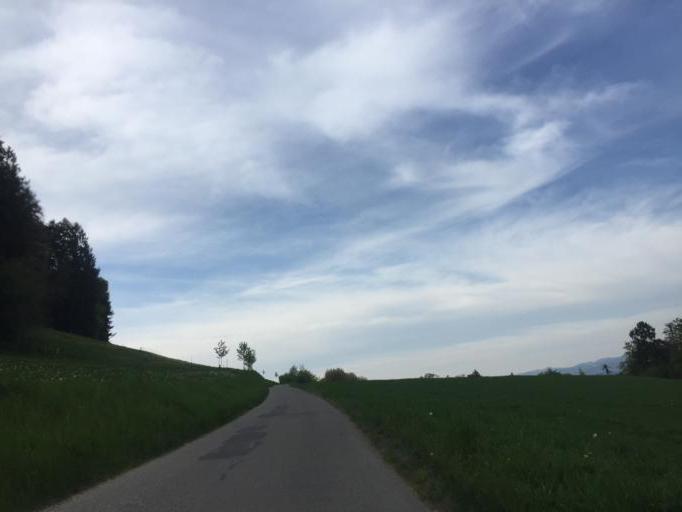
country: CH
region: Bern
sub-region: Bern-Mittelland District
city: Munsingen
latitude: 46.8549
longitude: 7.5486
